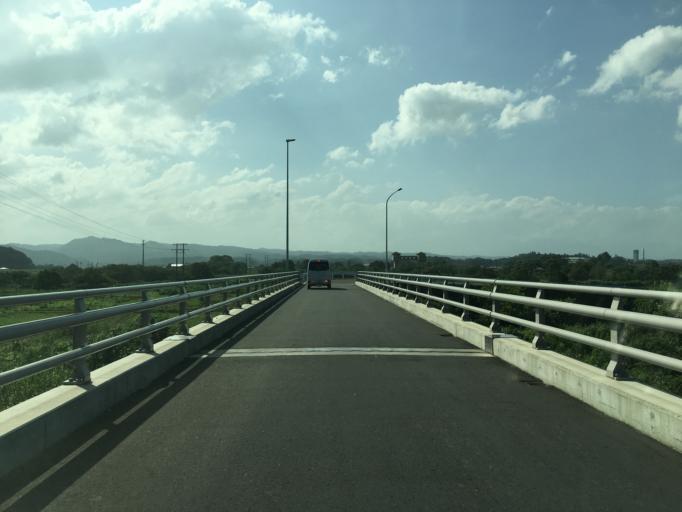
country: JP
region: Miyagi
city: Kakuda
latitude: 37.9597
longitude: 140.7901
